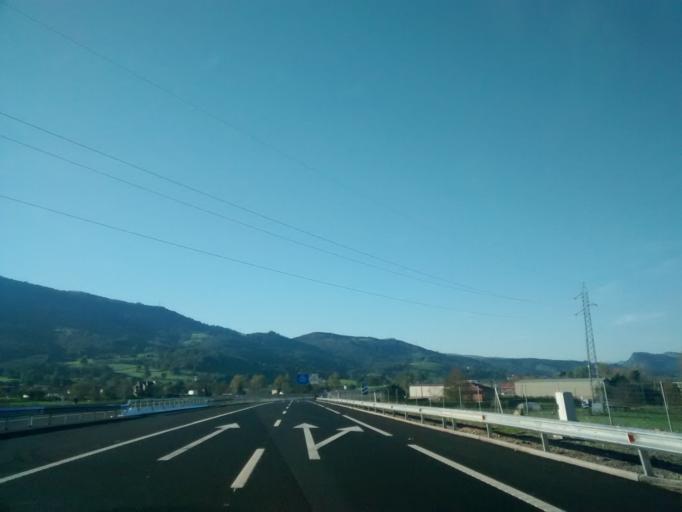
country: ES
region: Cantabria
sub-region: Provincia de Cantabria
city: Santa Maria de Cayon
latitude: 43.3157
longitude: -3.8735
